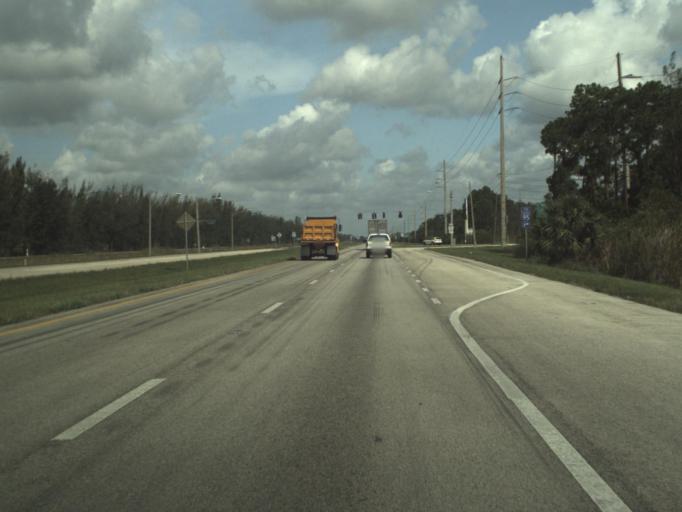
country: US
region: Florida
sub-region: Palm Beach County
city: Palm Beach Gardens
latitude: 26.8398
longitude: -80.1968
